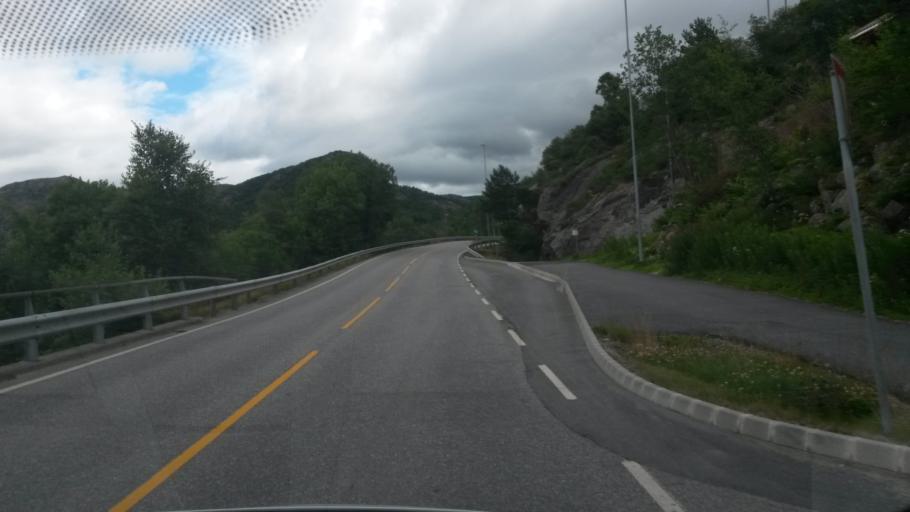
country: NO
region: Rogaland
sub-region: Sandnes
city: Sandnes
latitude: 58.8761
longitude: 5.7683
